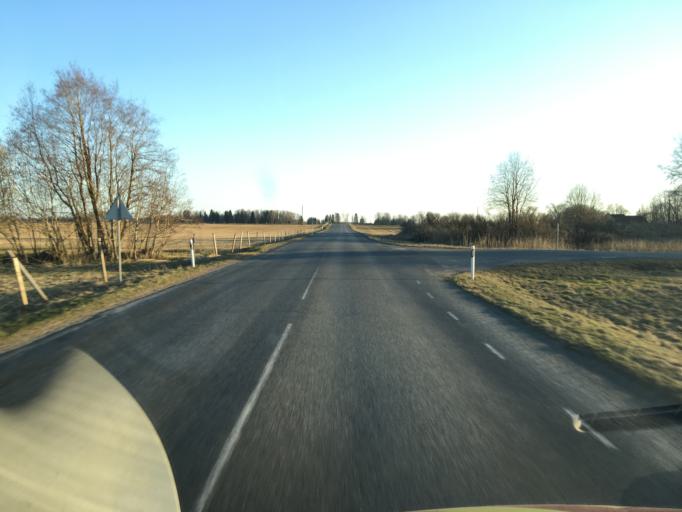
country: EE
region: Raplamaa
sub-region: Kehtna vald
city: Kehtna
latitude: 59.0208
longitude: 24.9261
